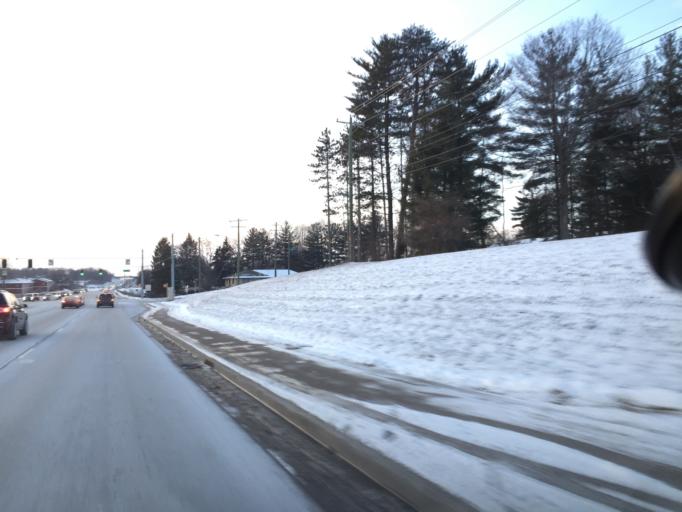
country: US
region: Indiana
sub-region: Monroe County
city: Bloomington
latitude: 39.1862
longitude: -86.5270
